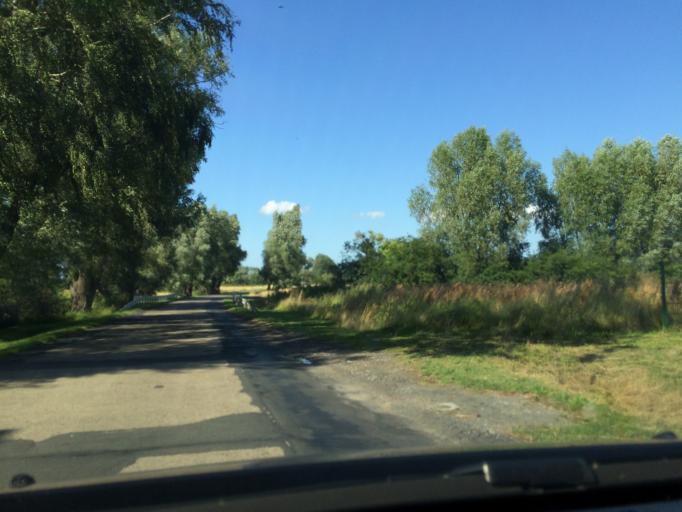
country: DE
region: Mecklenburg-Vorpommern
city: Niepars
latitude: 54.3485
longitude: 12.8978
